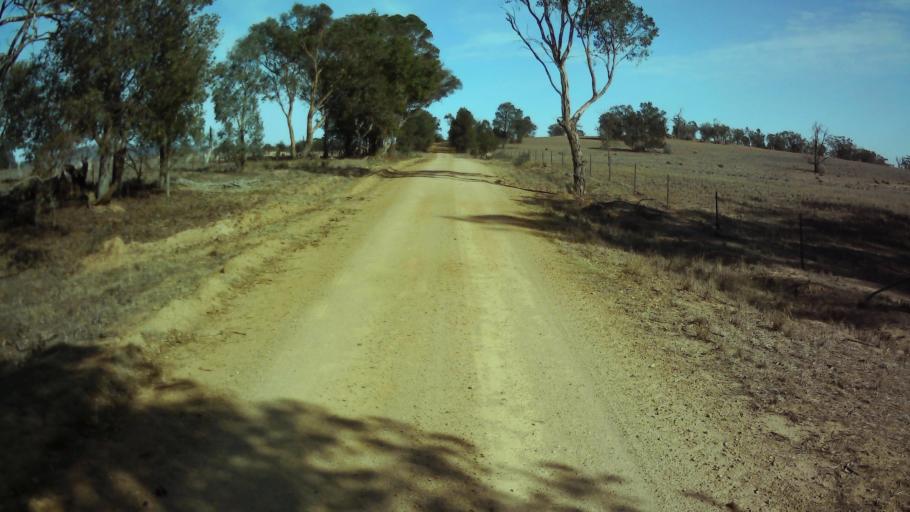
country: AU
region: New South Wales
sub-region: Weddin
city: Grenfell
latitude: -33.7579
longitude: 148.0283
